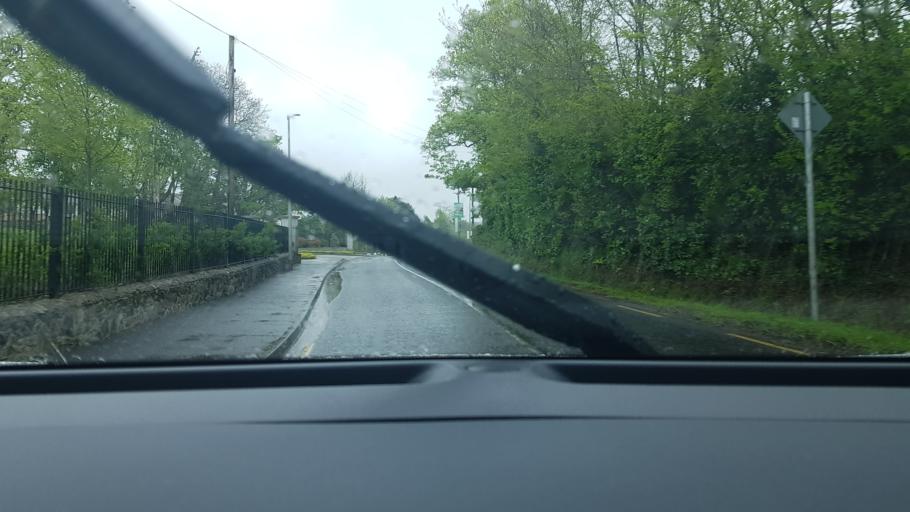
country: IE
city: Palmerstown
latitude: 53.3664
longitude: -6.3856
